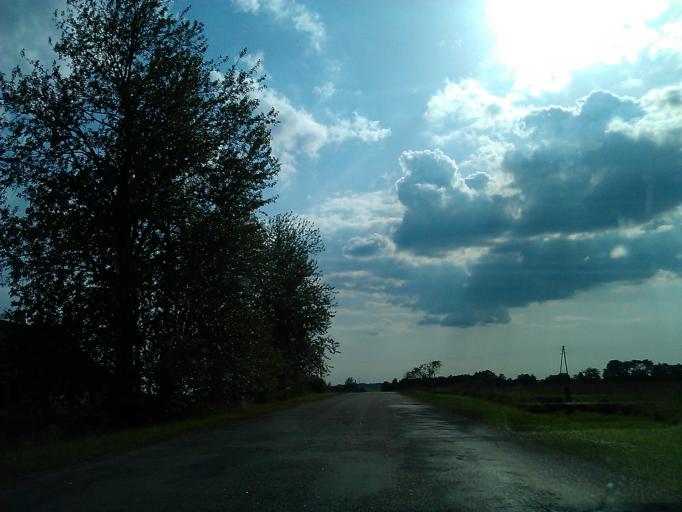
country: LV
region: Aizpute
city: Aizpute
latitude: 56.7297
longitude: 21.6586
